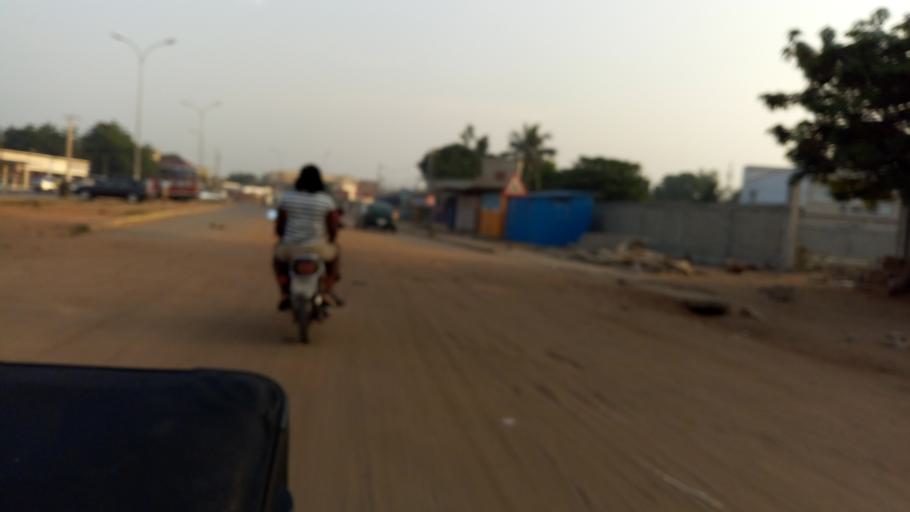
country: TG
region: Maritime
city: Lome
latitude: 6.1972
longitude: 1.1788
